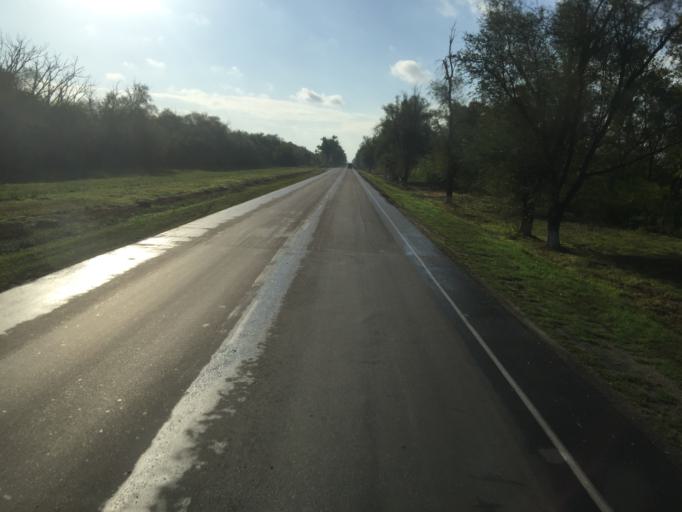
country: RU
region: Rostov
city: Yegorlykskaya
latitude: 46.5946
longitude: 40.6245
